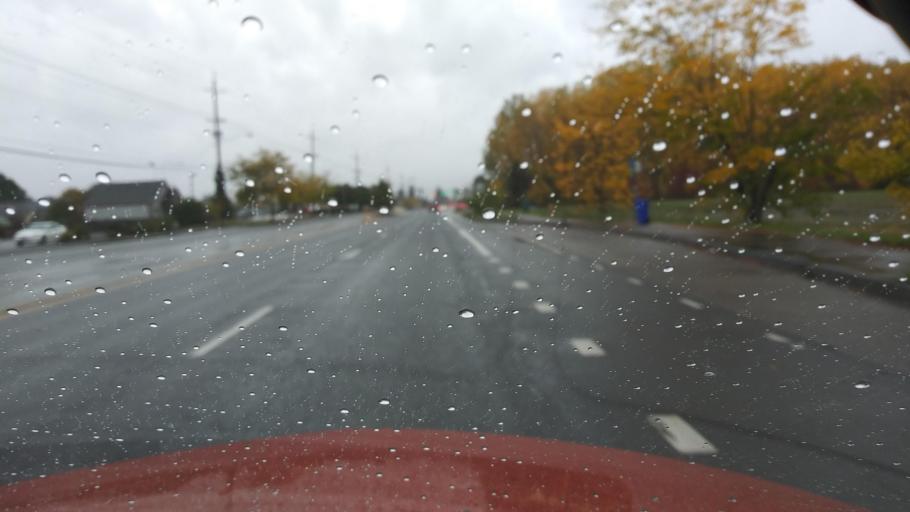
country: US
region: Oregon
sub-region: Washington County
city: Cornelius
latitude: 45.5202
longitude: -123.0401
